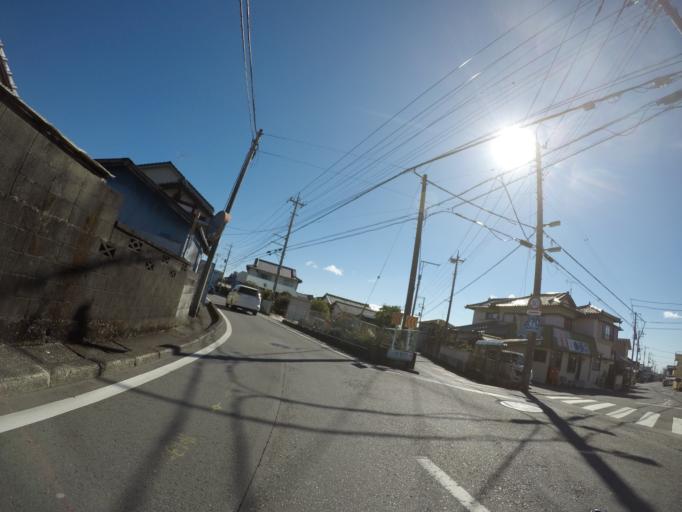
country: JP
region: Shizuoka
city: Fuji
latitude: 35.1639
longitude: 138.7328
